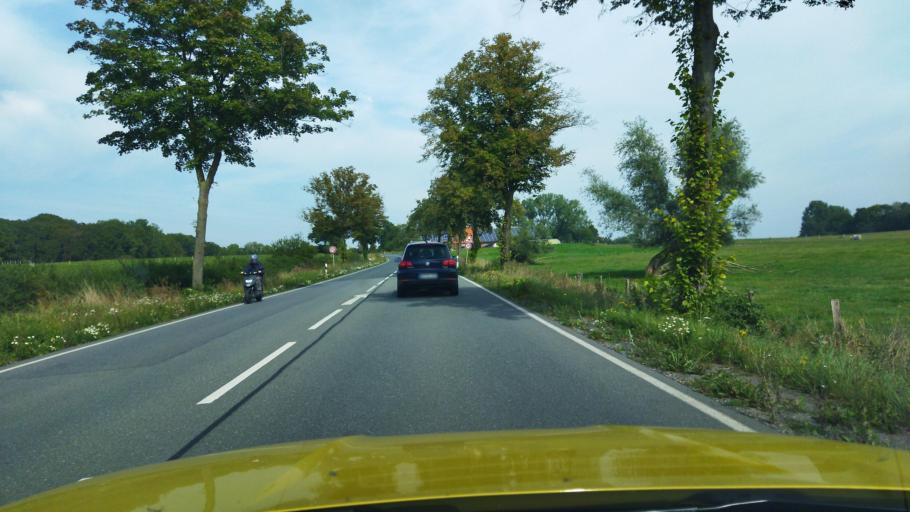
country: DE
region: North Rhine-Westphalia
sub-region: Regierungsbezirk Munster
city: Ennigerloh
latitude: 51.8716
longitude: 8.0323
